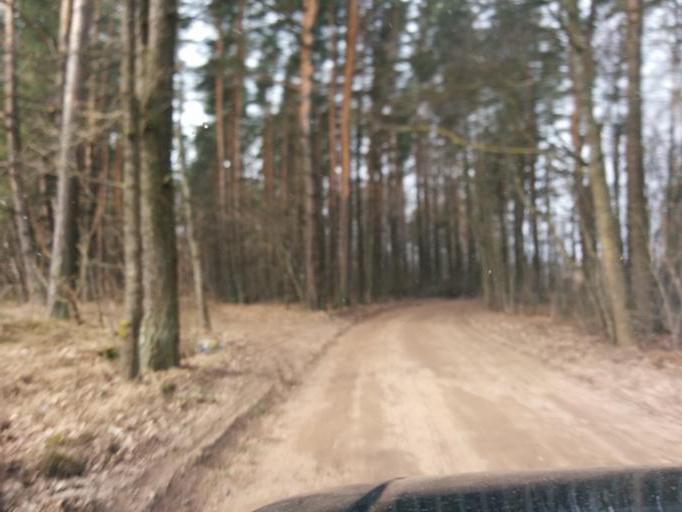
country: LV
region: Kekava
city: Kekava
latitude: 56.8159
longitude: 24.2631
